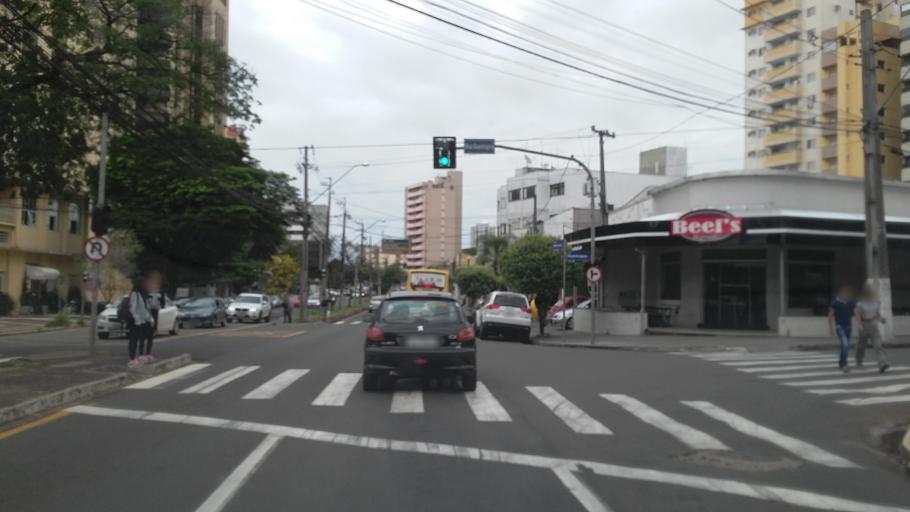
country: BR
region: Parana
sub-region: Londrina
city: Londrina
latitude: -23.3207
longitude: -51.1667
